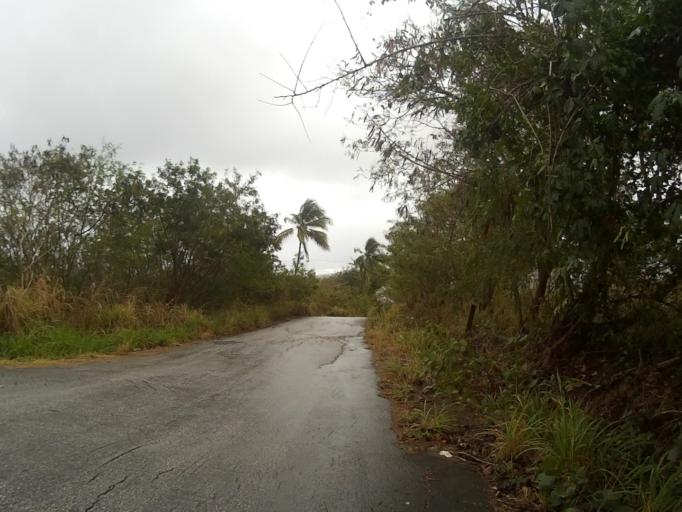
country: BB
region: Saint Andrew
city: Greenland
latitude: 13.2734
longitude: -59.5785
